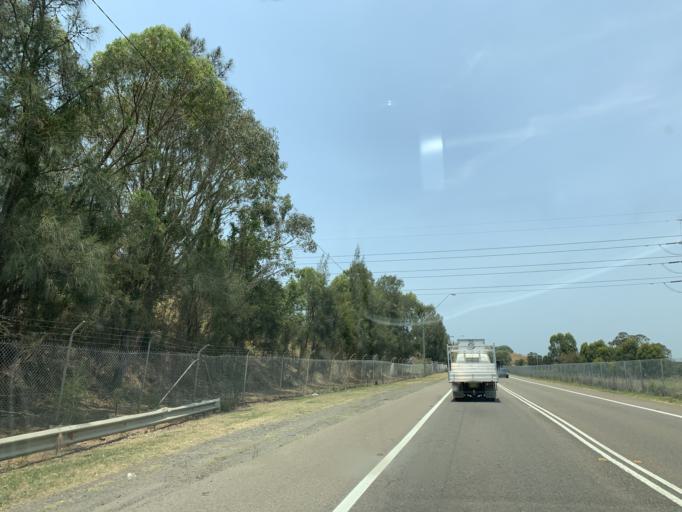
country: AU
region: New South Wales
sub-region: Blacktown
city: Doonside
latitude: -33.8042
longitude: 150.8644
